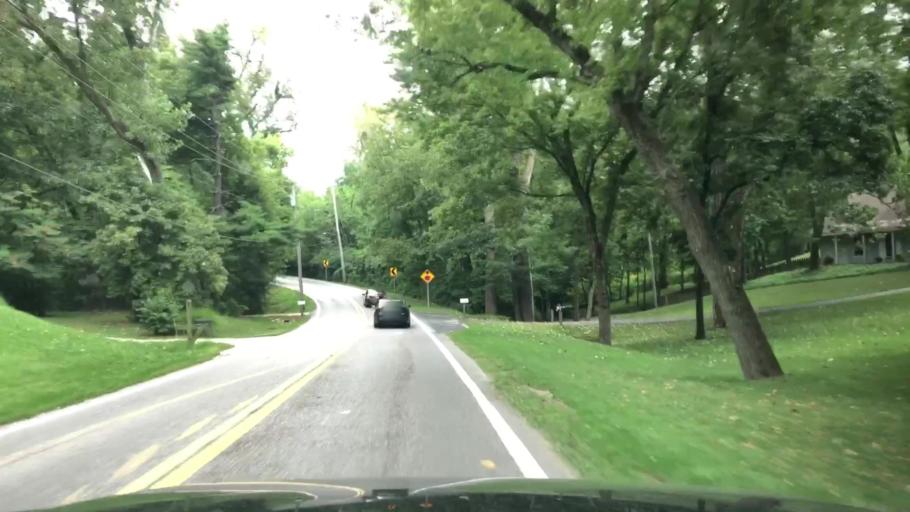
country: US
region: Missouri
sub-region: Saint Louis County
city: Hazelwood
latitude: 38.8091
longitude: -90.3840
